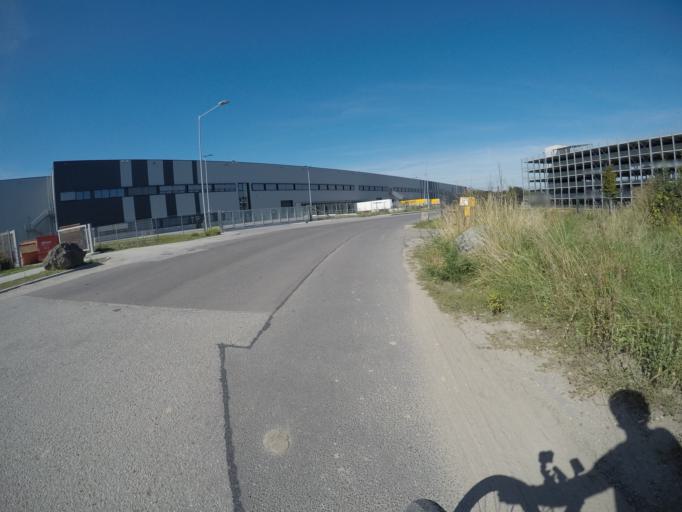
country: DE
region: Hesse
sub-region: Regierungsbezirk Darmstadt
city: Biblis
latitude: 49.6947
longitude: 8.4510
